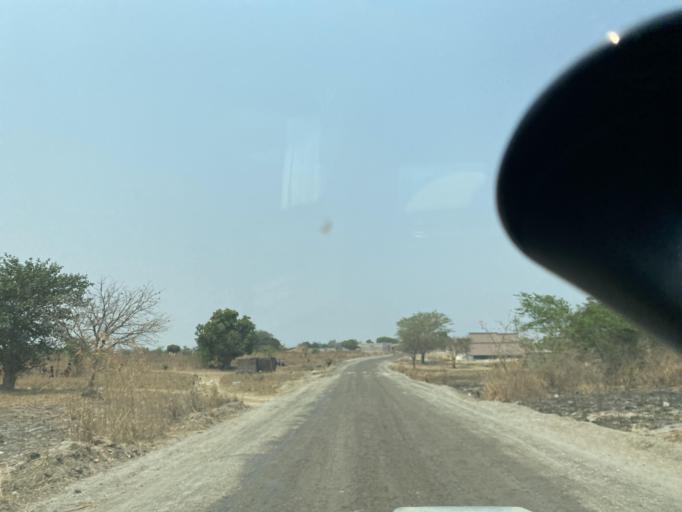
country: ZM
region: Lusaka
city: Lusaka
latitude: -15.5610
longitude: 28.4229
